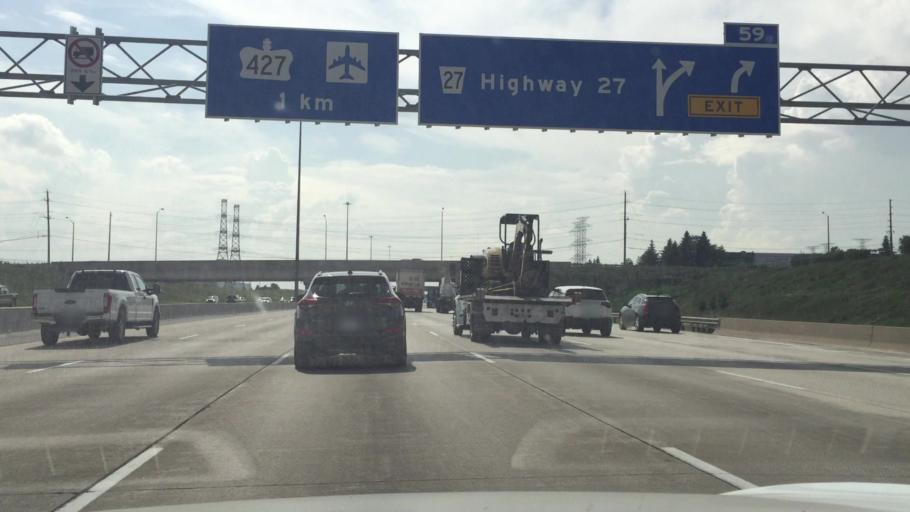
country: CA
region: Ontario
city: Etobicoke
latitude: 43.7617
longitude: -79.6038
